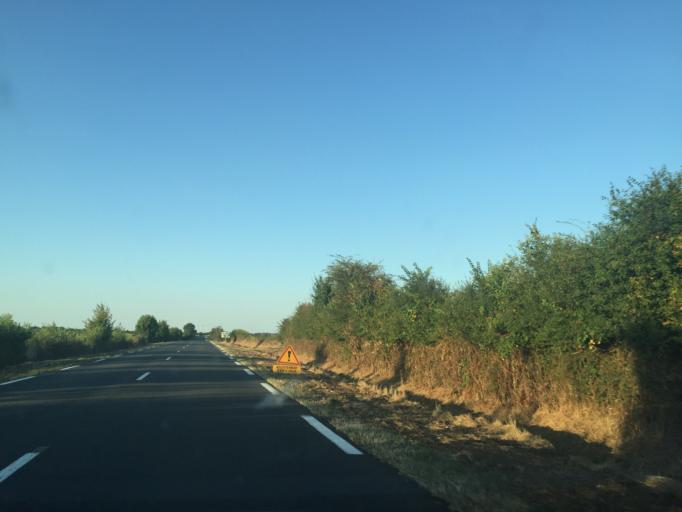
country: FR
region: Poitou-Charentes
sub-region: Departement de la Vienne
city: Saint-Sauvant
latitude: 46.3772
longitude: 0.0373
